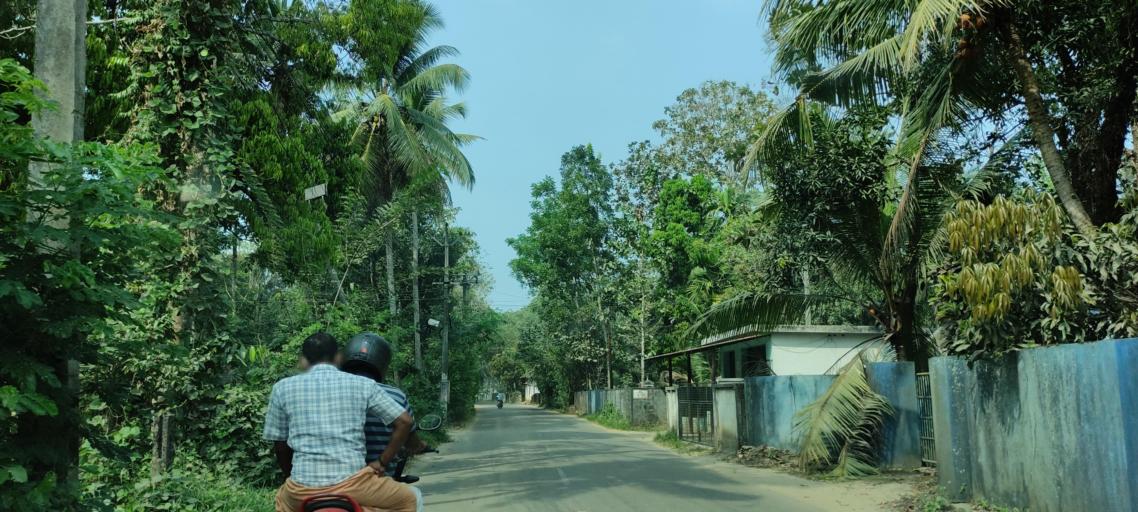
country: IN
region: Kerala
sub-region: Kottayam
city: Vaikam
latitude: 9.7359
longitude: 76.4135
